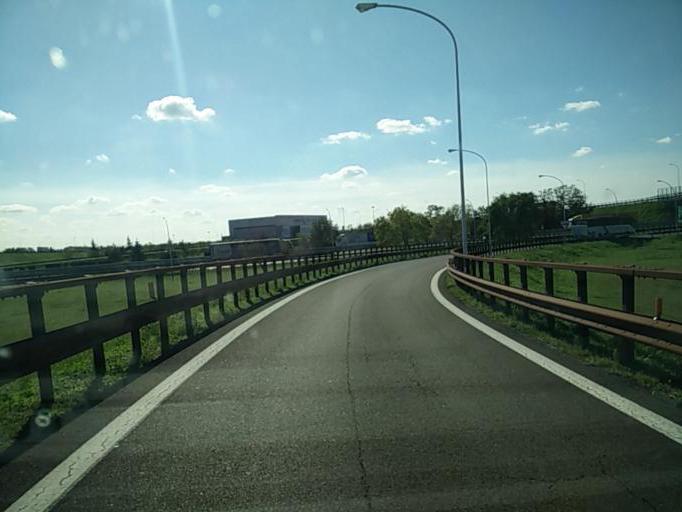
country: IT
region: Veneto
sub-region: Provincia di Verona
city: Dossobuono
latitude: 45.4096
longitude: 10.9118
